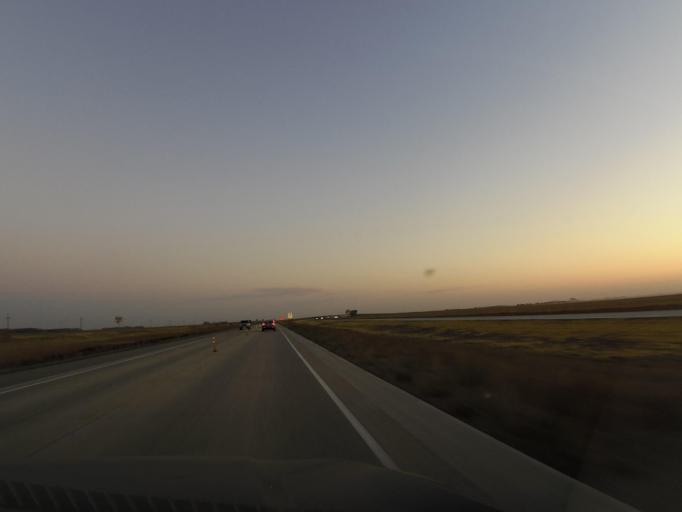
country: US
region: North Dakota
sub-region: Traill County
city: Hillsboro
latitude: 47.2078
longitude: -96.9922
